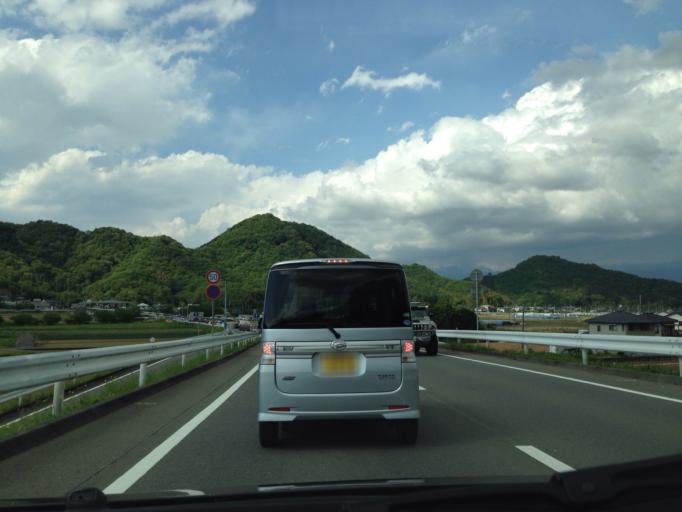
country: JP
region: Shizuoka
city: Mishima
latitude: 35.0525
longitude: 138.9239
